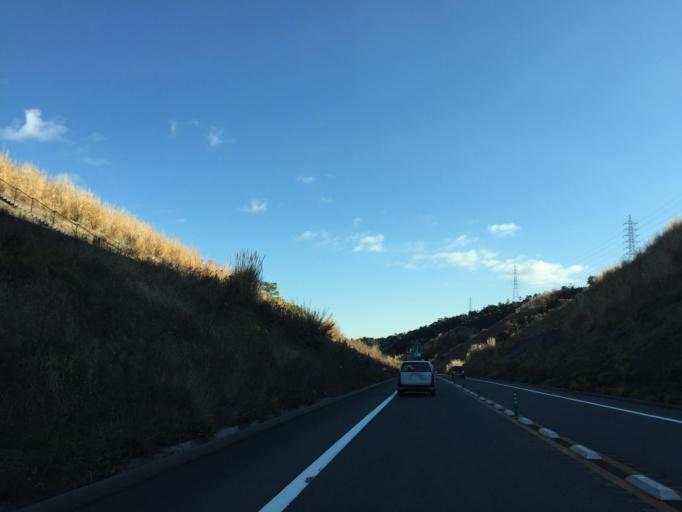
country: JP
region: Wakayama
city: Wakayama-shi
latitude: 34.3201
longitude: 135.1677
